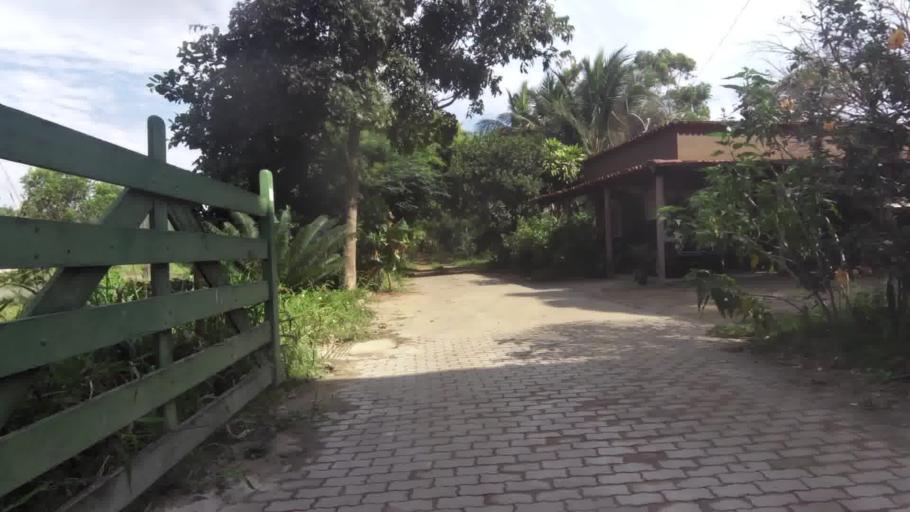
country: BR
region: Espirito Santo
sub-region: Piuma
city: Piuma
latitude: -20.8525
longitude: -40.7529
